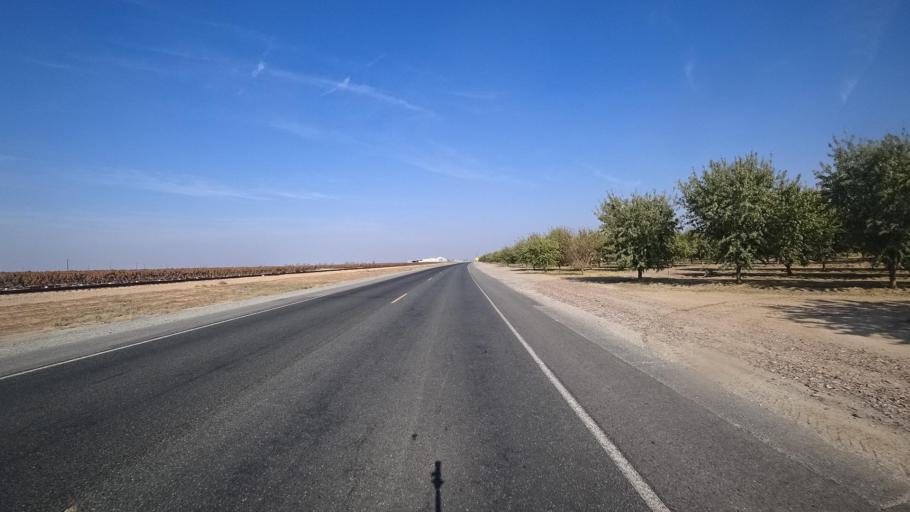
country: US
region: California
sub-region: Kern County
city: McFarland
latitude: 35.6626
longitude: -119.1938
